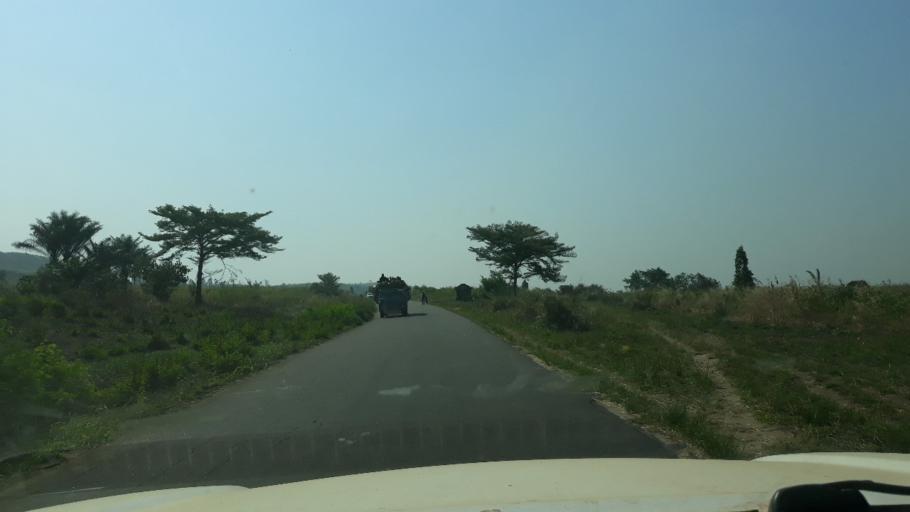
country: CD
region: South Kivu
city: Uvira
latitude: -3.2093
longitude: 29.1641
